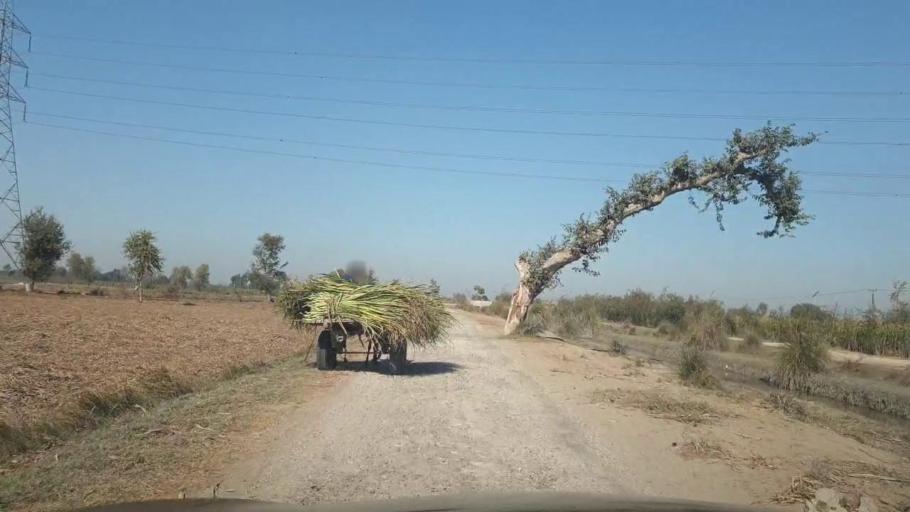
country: PK
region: Sindh
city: Ghotki
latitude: 27.9916
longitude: 69.4275
